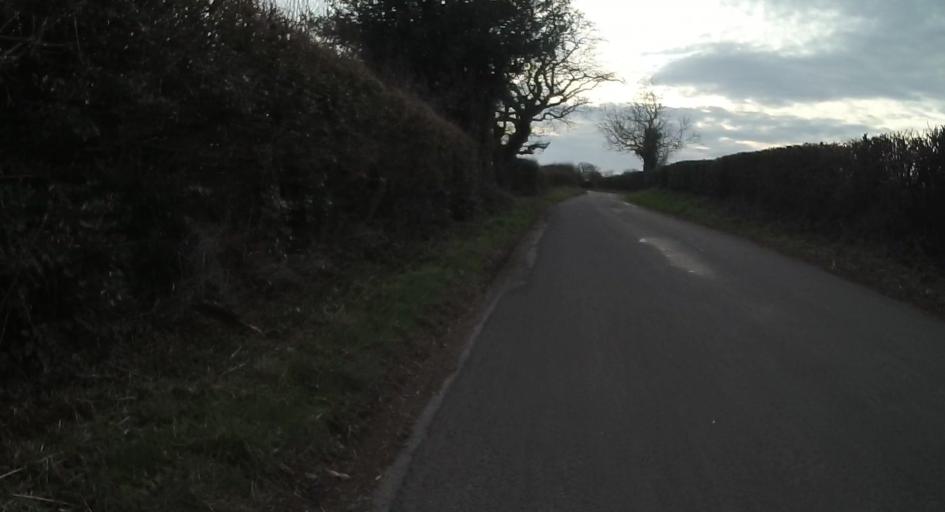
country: GB
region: England
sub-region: West Berkshire
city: Theale
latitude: 51.4107
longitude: -1.0693
